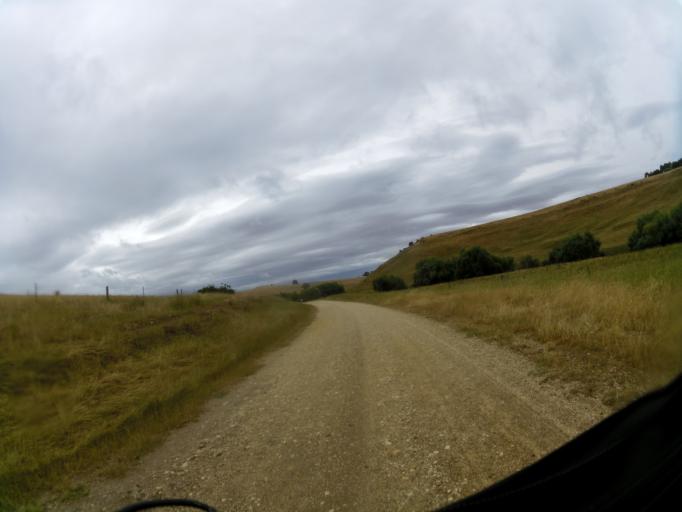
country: AU
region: Victoria
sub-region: Mount Alexander
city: Castlemaine
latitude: -37.2047
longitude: 144.0223
